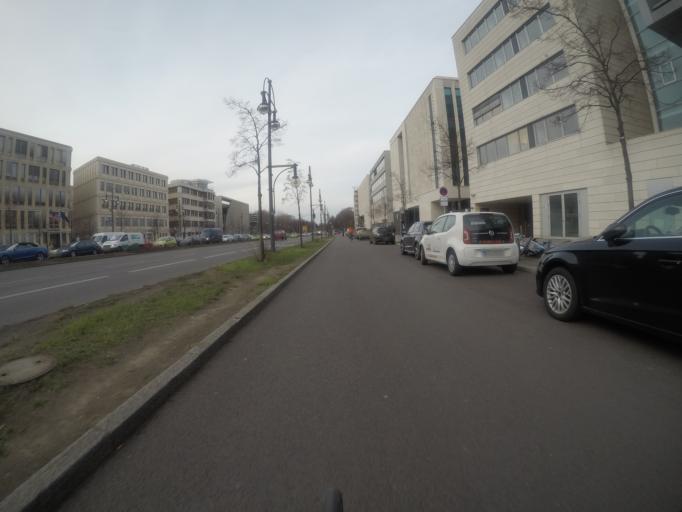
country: DE
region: Berlin
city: Hansaviertel
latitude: 52.5070
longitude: 13.3522
